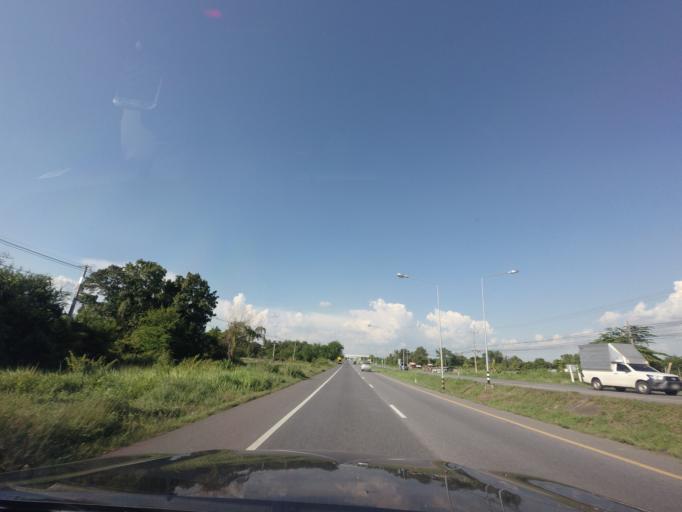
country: TH
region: Khon Kaen
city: Non Sila
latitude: 15.9484
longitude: 102.6816
